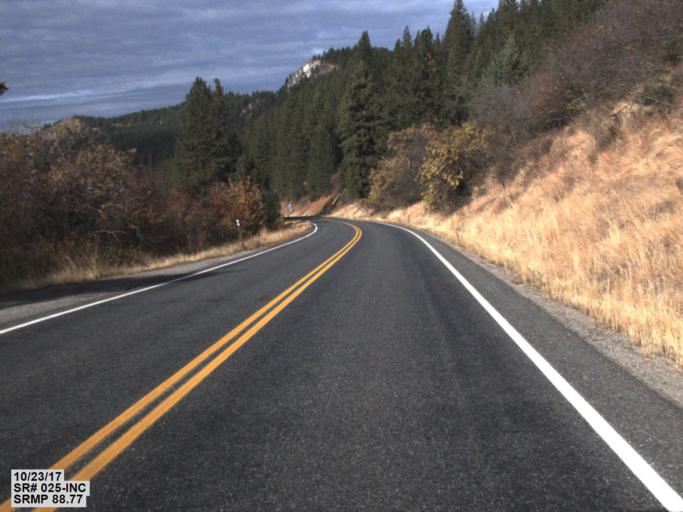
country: US
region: Washington
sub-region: Stevens County
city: Kettle Falls
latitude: 48.6814
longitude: -118.0148
